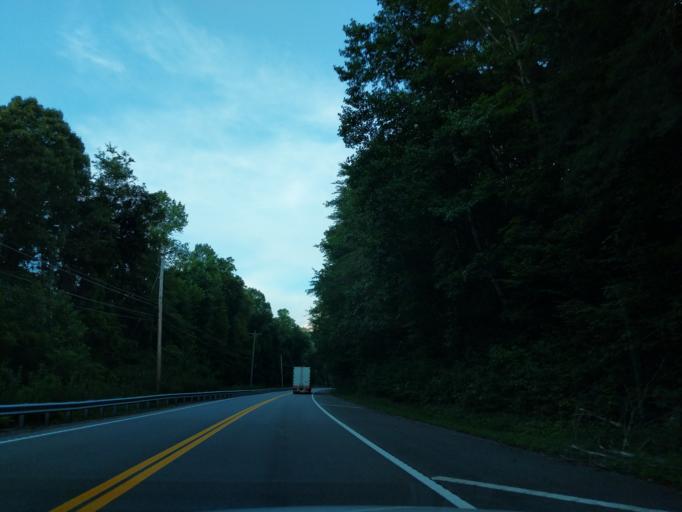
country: US
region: Tennessee
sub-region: Hamilton County
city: Lookout Mountain
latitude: 35.0329
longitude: -85.4285
